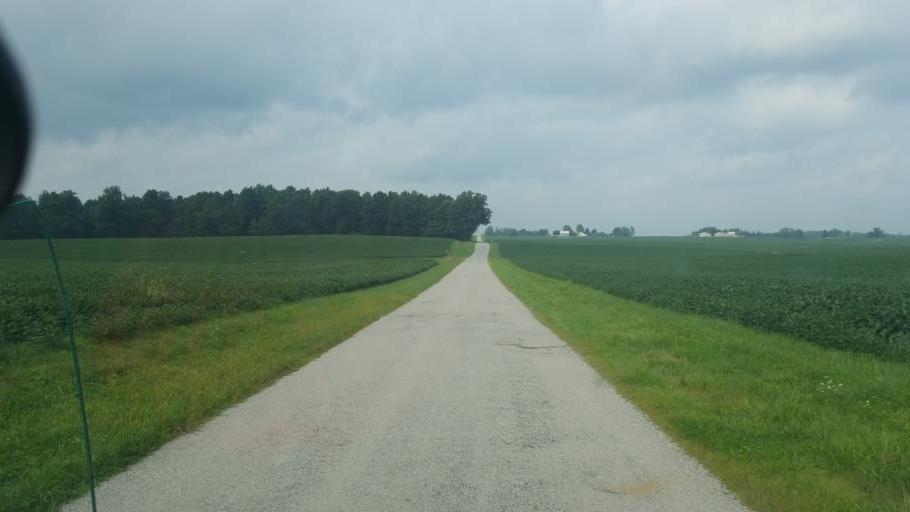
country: US
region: Ohio
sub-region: Huron County
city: New London
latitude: 41.0777
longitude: -82.4619
